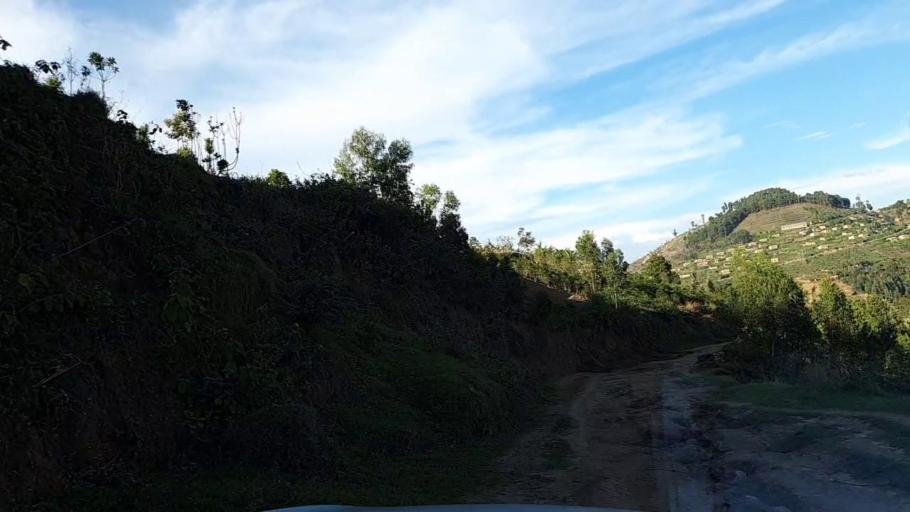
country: RW
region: Southern Province
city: Gikongoro
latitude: -2.4081
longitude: 29.5233
